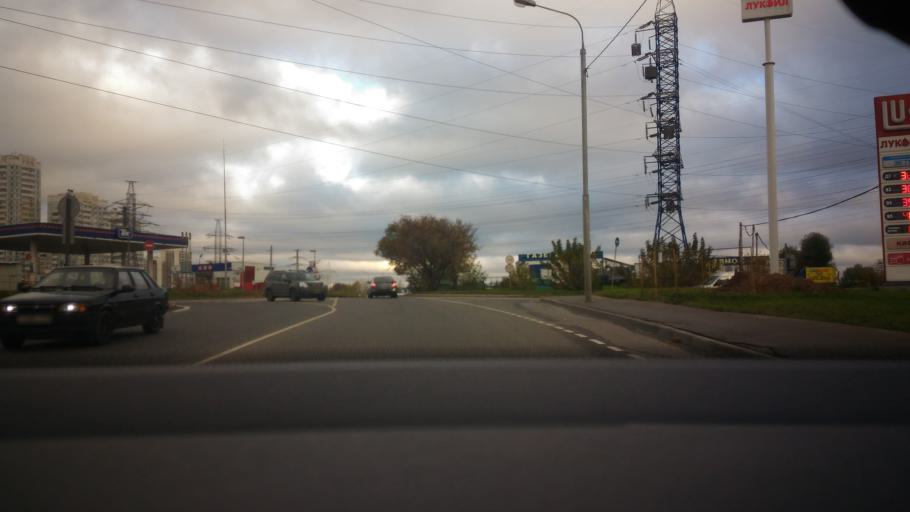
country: RU
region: Moscow
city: Strogino
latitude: 55.8352
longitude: 37.3982
